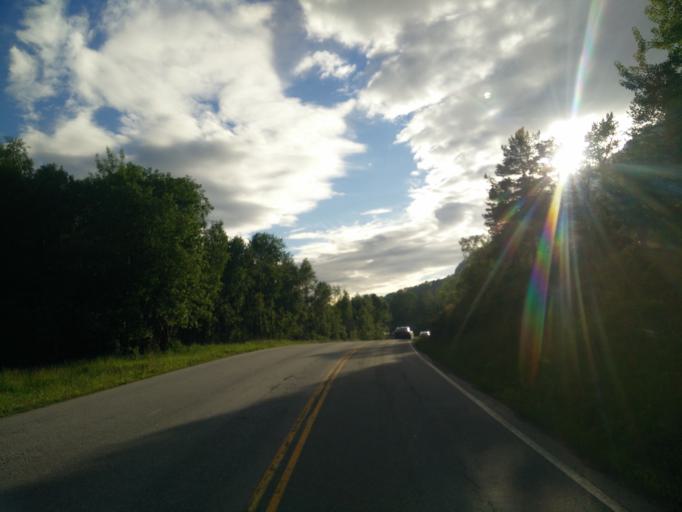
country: NO
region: More og Romsdal
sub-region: Tingvoll
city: Tingvoll
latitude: 63.0518
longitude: 8.1214
